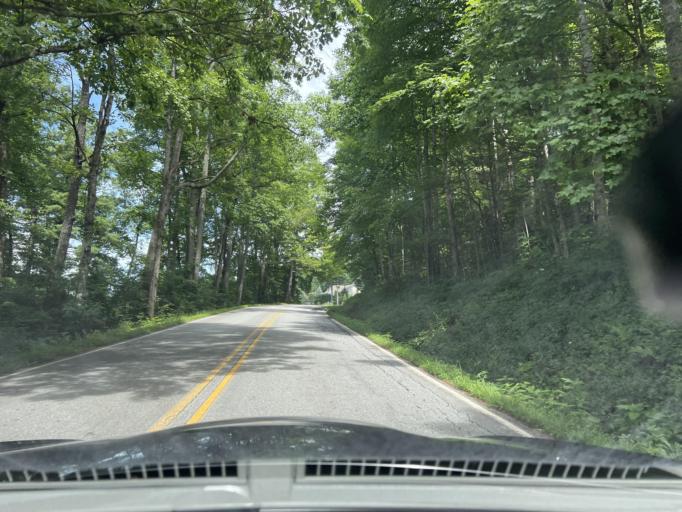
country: US
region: North Carolina
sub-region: Henderson County
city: Edneyville
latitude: 35.3824
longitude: -82.3142
